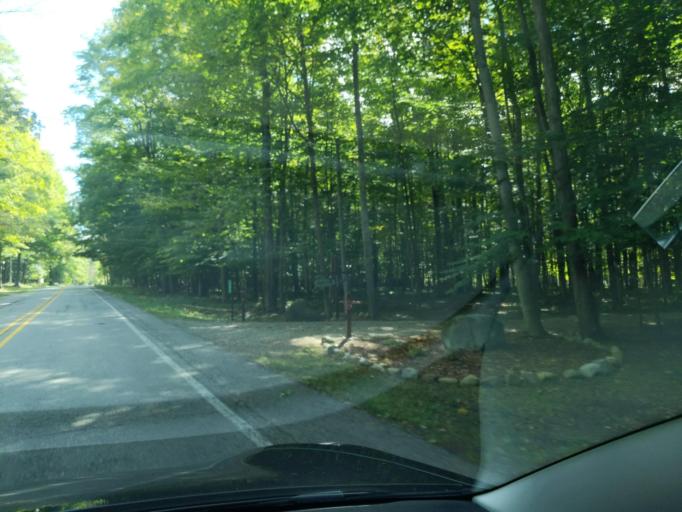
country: US
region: Michigan
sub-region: Antrim County
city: Bellaire
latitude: 45.0727
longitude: -85.3190
